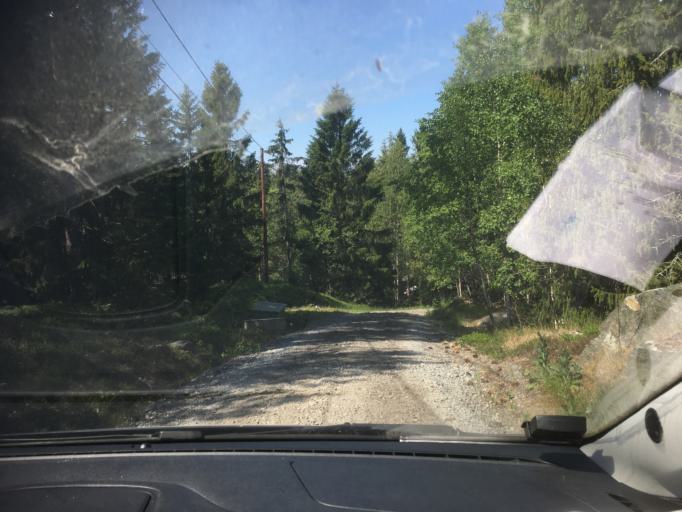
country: SE
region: Stockholm
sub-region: Haninge Kommun
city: Jordbro
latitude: 59.0110
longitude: 18.1640
